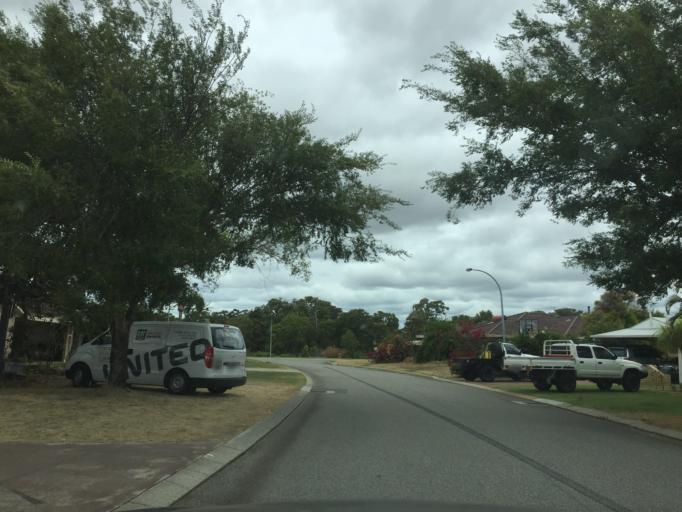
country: AU
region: Western Australia
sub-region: Gosnells
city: Thornlie
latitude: -32.0740
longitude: 115.9583
